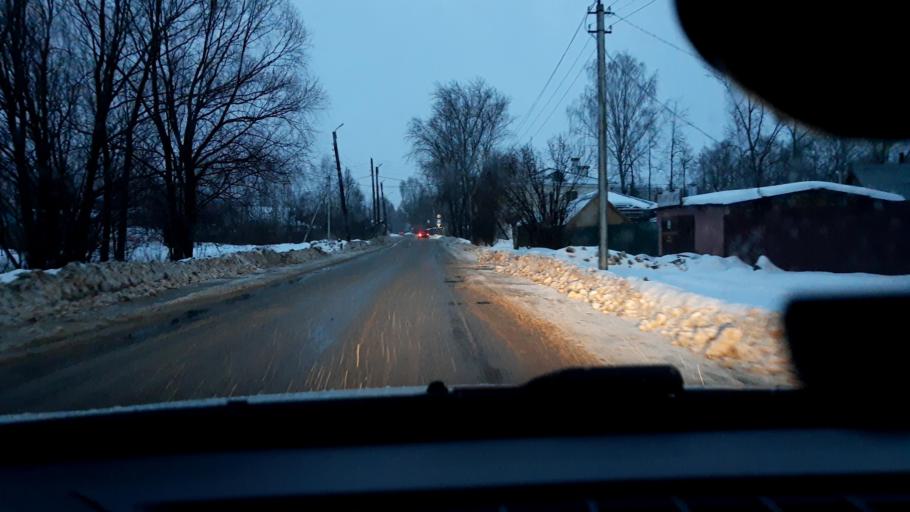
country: RU
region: Nizjnij Novgorod
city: Bogorodsk
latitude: 56.1067
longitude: 43.4894
